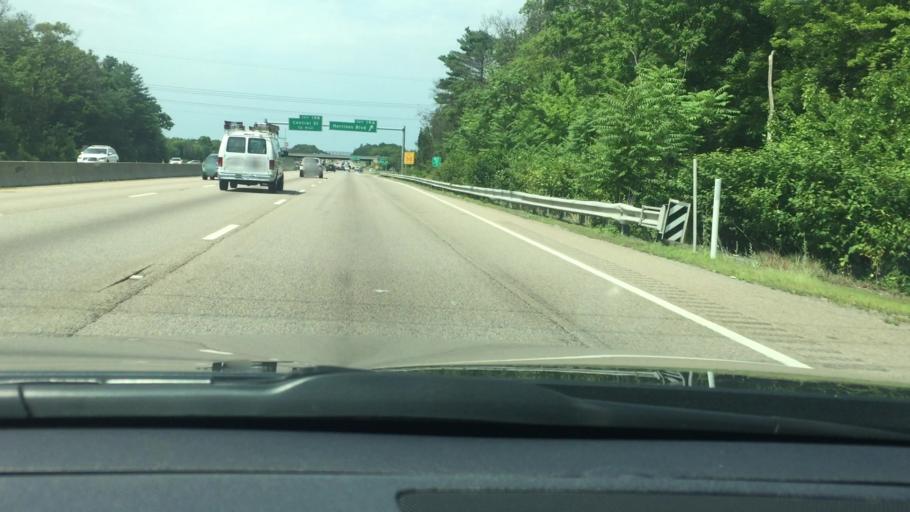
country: US
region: Massachusetts
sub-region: Norfolk County
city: Avon
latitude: 42.1209
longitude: -71.0613
